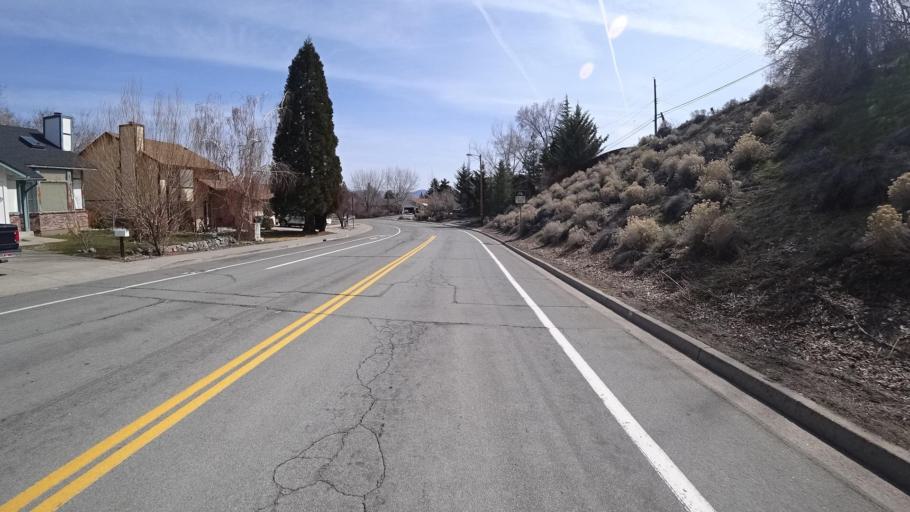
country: US
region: Nevada
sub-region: Washoe County
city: Reno
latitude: 39.5448
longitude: -119.8414
